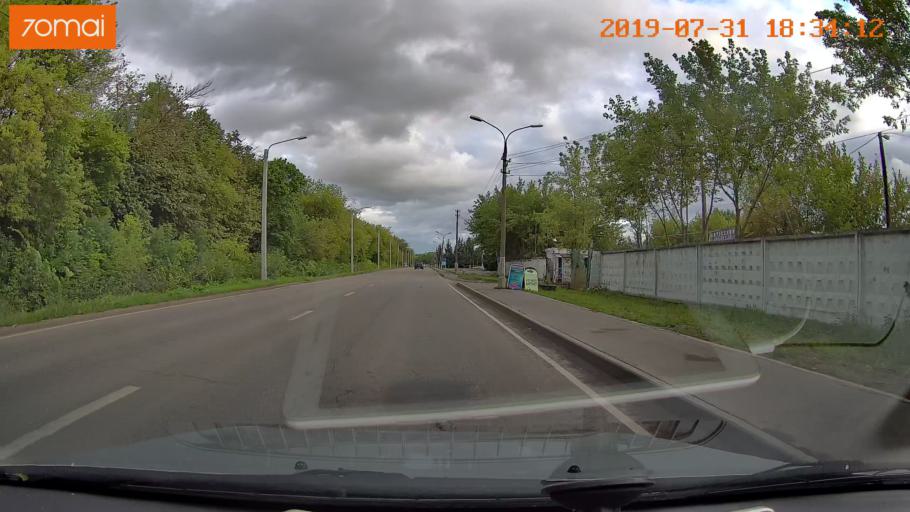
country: RU
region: Moskovskaya
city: Voskresensk
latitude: 55.3067
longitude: 38.6583
